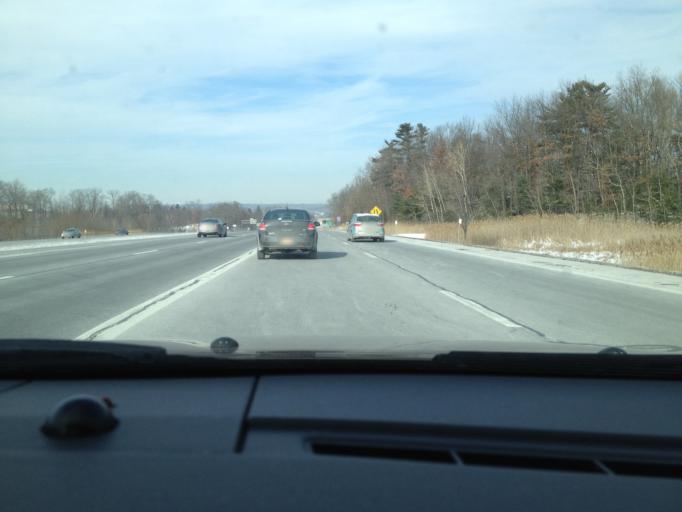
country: US
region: New York
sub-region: Rensselaer County
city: Rensselaer
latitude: 42.6519
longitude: -73.7149
